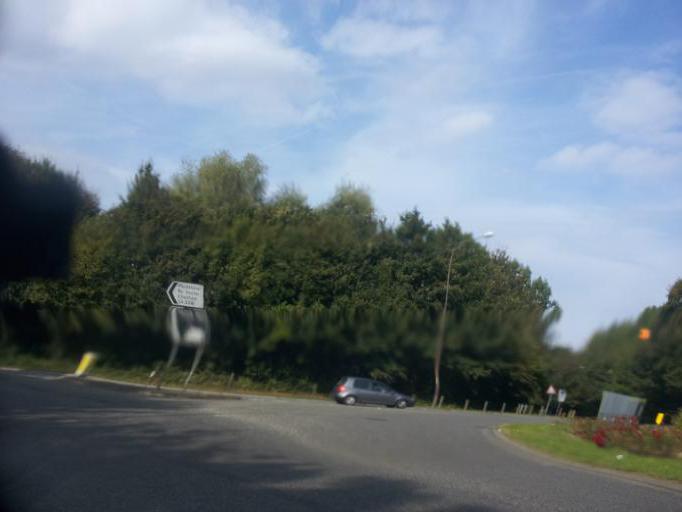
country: GB
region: England
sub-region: Kent
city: Boxley
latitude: 51.3261
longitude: 0.5430
